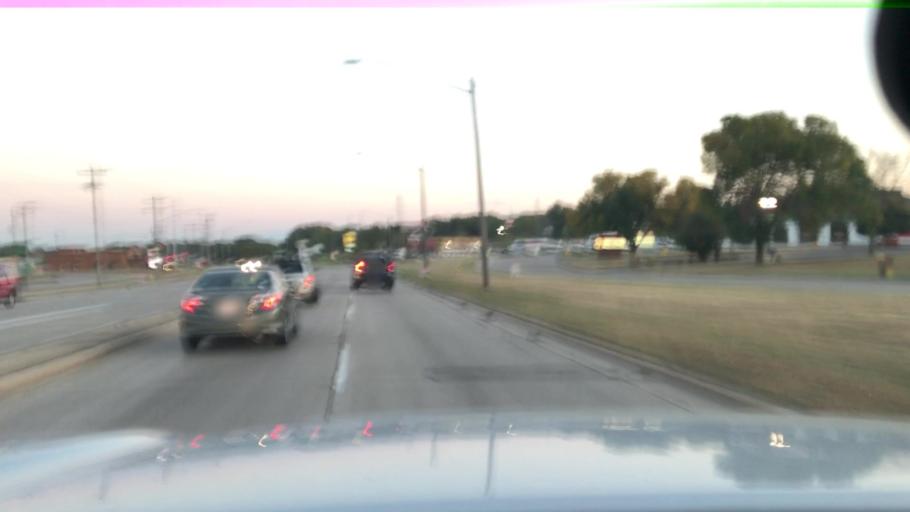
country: US
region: Wisconsin
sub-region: Brown County
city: Allouez
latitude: 44.4849
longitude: -87.9709
